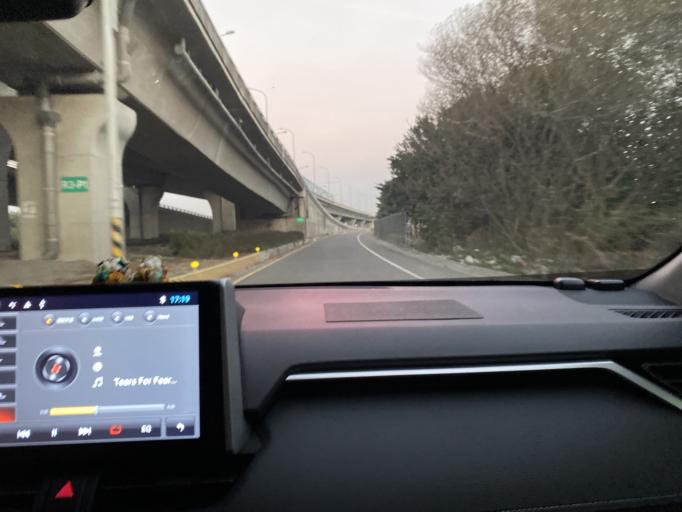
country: TW
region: Taiwan
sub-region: Changhua
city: Chang-hua
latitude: 23.9705
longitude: 120.3456
